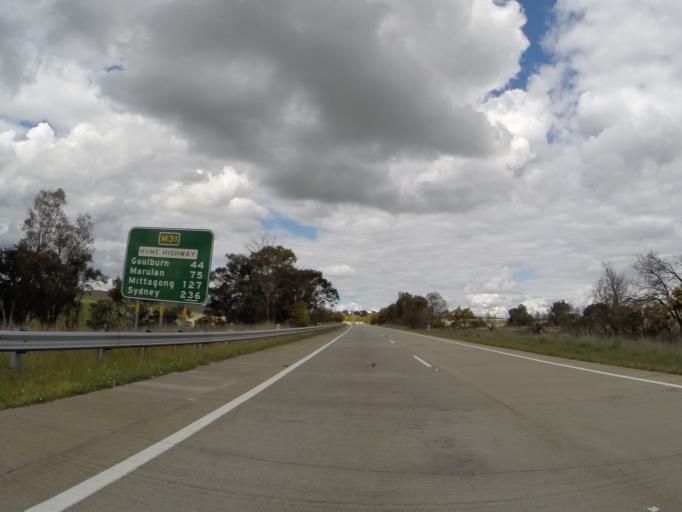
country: AU
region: New South Wales
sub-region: Yass Valley
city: Gundaroo
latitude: -34.7975
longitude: 149.2795
